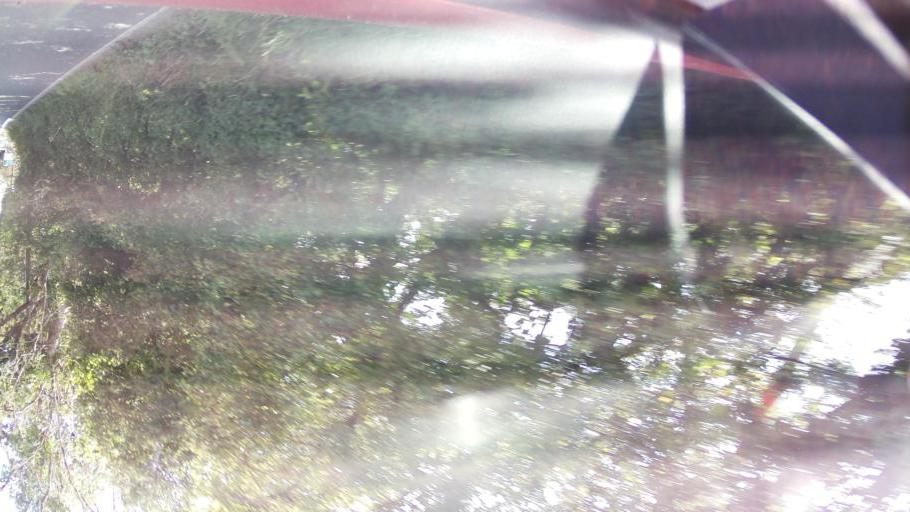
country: GB
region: England
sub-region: Cornwall
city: Saltash
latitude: 50.4241
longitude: -4.2444
